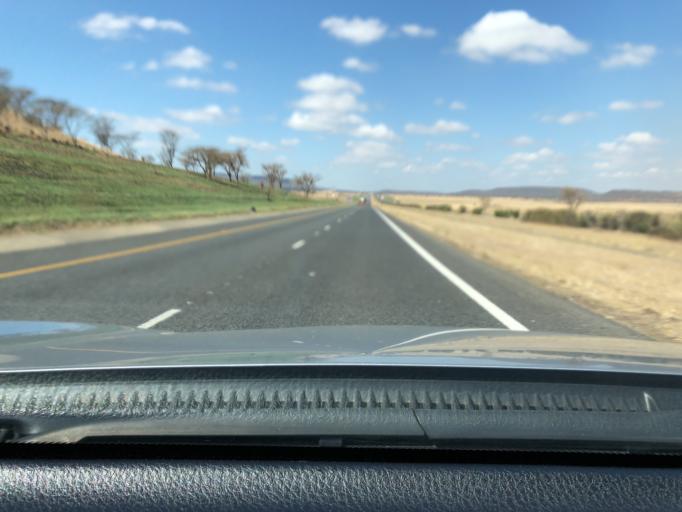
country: ZA
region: KwaZulu-Natal
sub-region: uThukela District Municipality
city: Ladysmith
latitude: -28.7893
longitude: 29.6831
